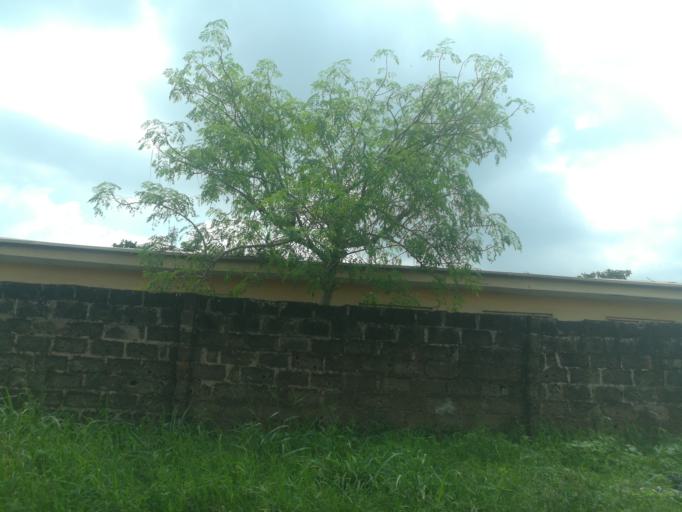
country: NG
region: Oyo
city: Ibadan
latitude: 7.3601
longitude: 3.8677
